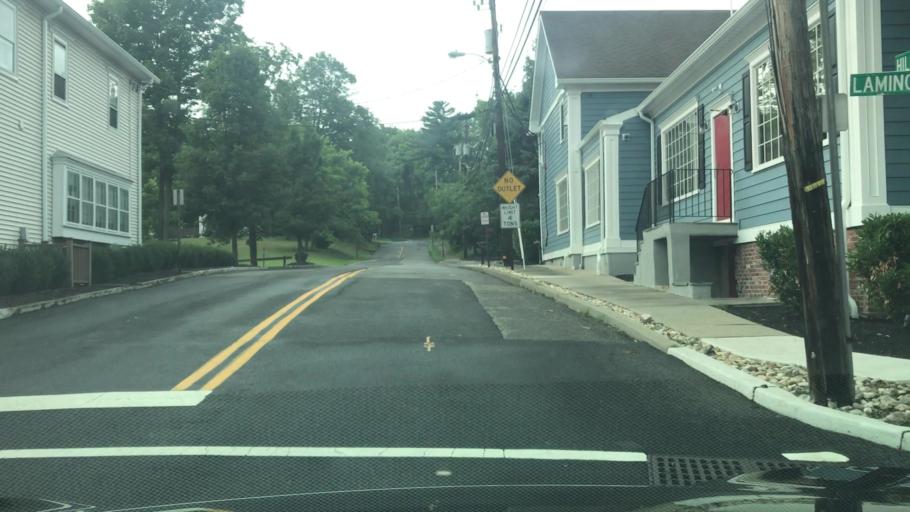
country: US
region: New Jersey
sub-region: Somerset County
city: Bedminster
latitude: 40.6806
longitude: -74.6457
